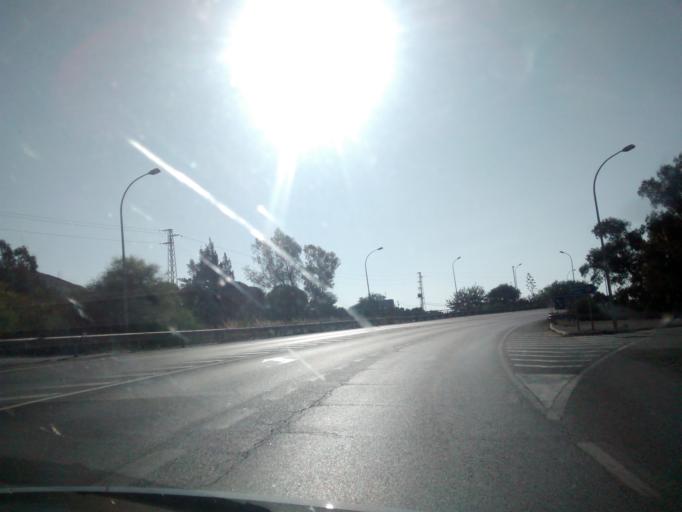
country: ES
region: Andalusia
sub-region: Provincia de Cadiz
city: Jerez de la Frontera
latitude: 36.6542
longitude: -6.0861
